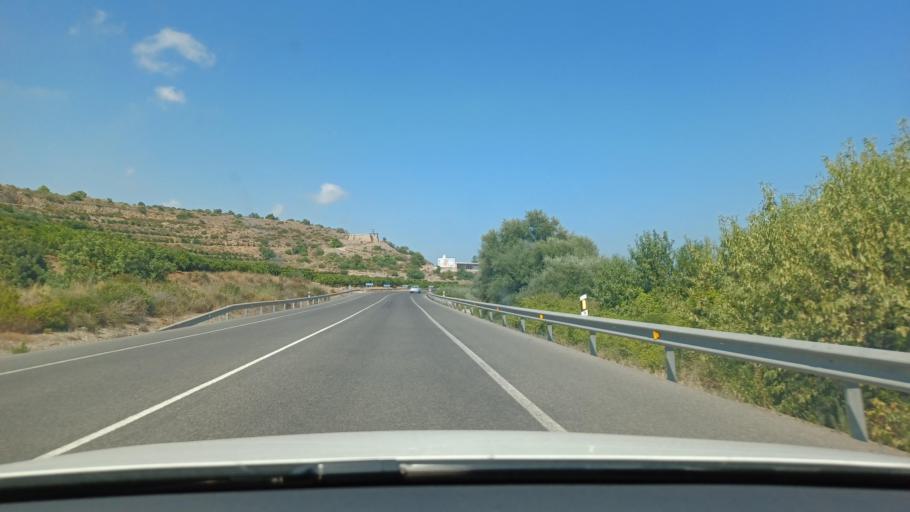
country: ES
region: Valencia
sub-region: Provincia de Castello
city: Chilches
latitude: 39.7745
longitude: -0.2031
